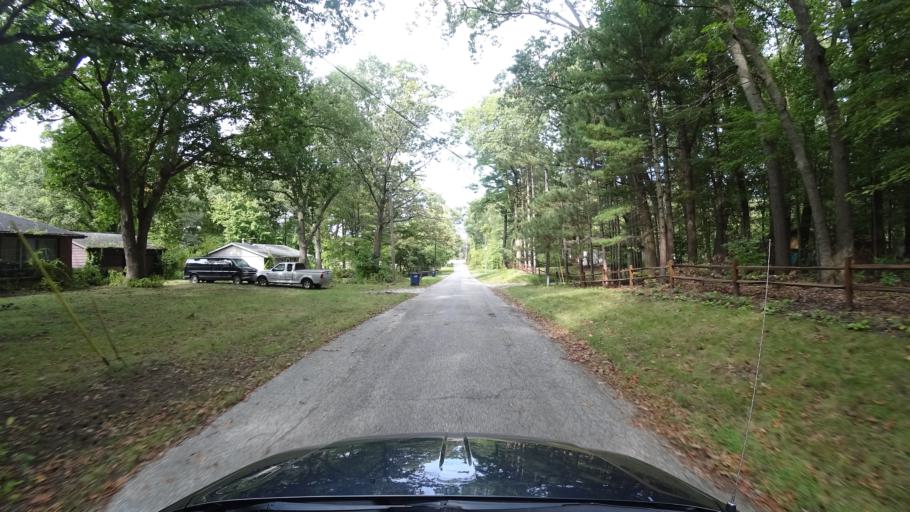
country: US
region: Indiana
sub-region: LaPorte County
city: Long Beach
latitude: 41.7356
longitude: -86.8459
